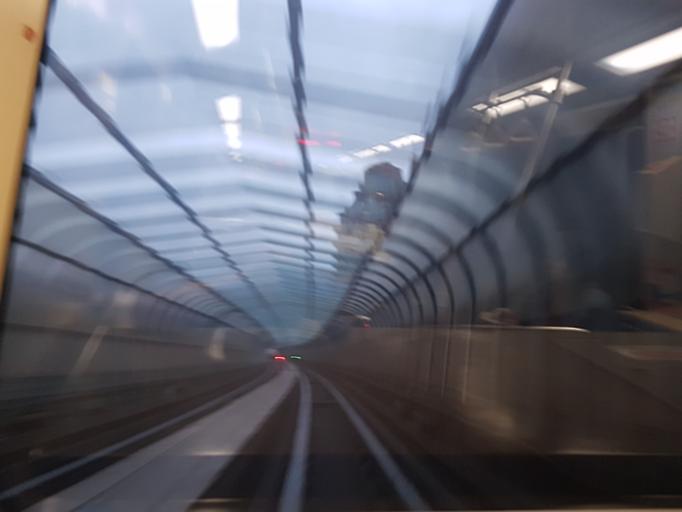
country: TW
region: Taipei
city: Taipei
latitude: 25.0716
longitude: 121.6097
